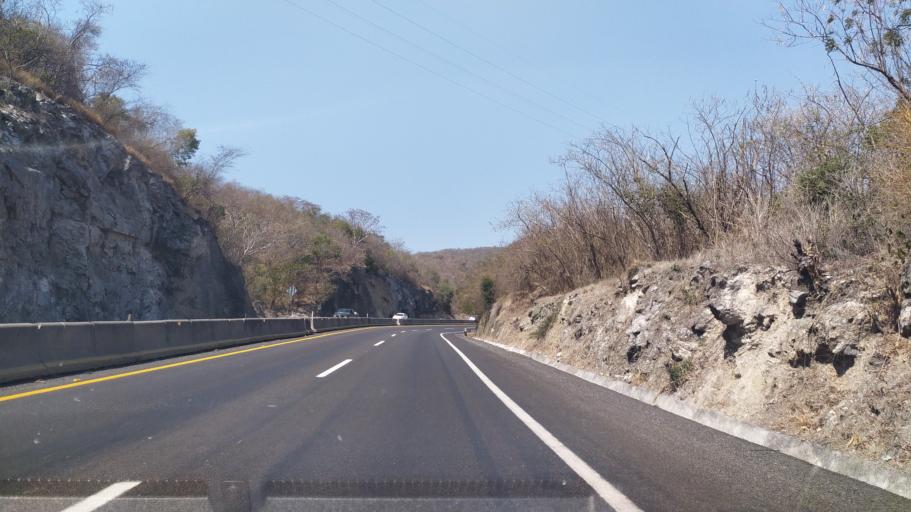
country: MX
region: Colima
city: Ixtlahuacan
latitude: 19.0621
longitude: -103.7855
